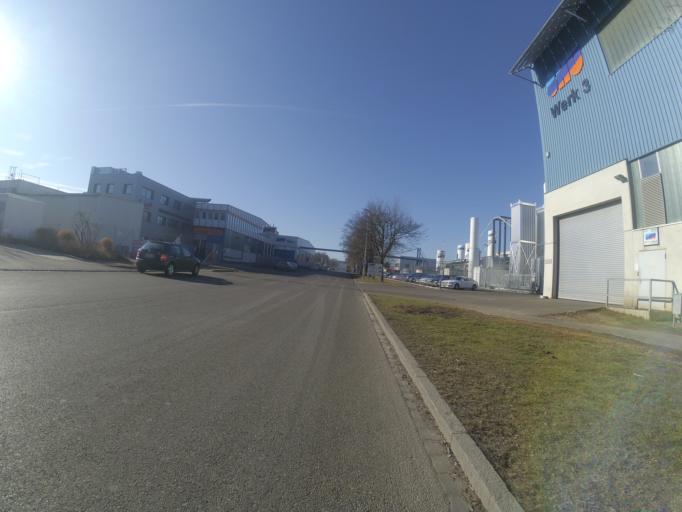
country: DE
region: Baden-Wuerttemberg
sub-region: Tuebingen Region
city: Ulm
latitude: 48.3605
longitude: 9.9452
